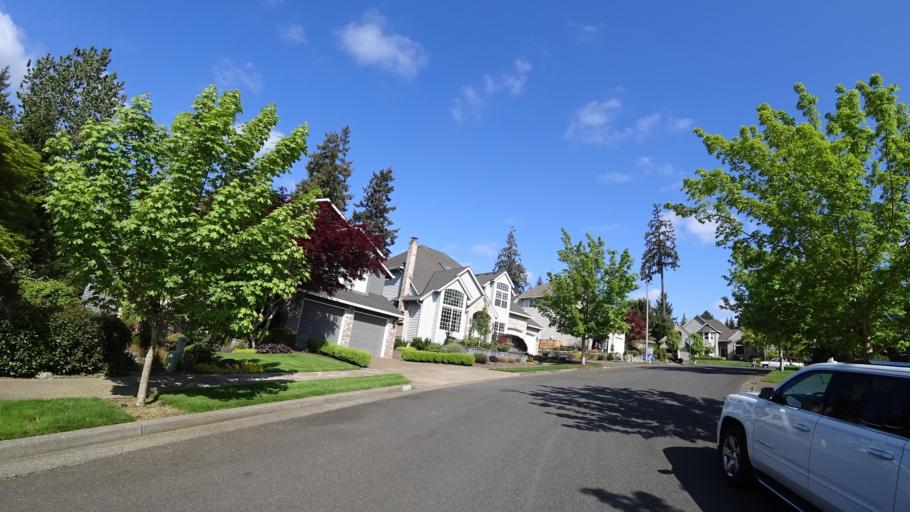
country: US
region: Oregon
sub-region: Washington County
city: King City
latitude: 45.4425
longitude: -122.8340
